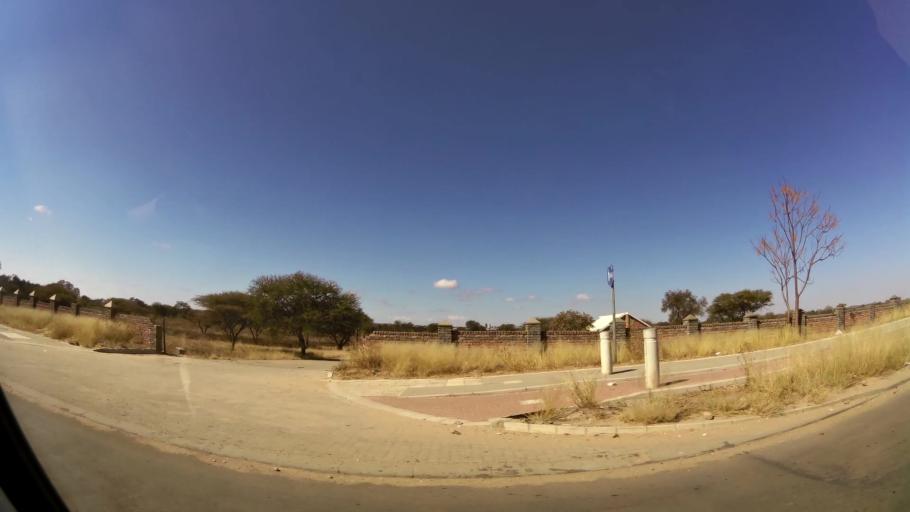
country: ZA
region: Limpopo
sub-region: Capricorn District Municipality
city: Polokwane
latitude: -23.8911
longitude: 29.4234
